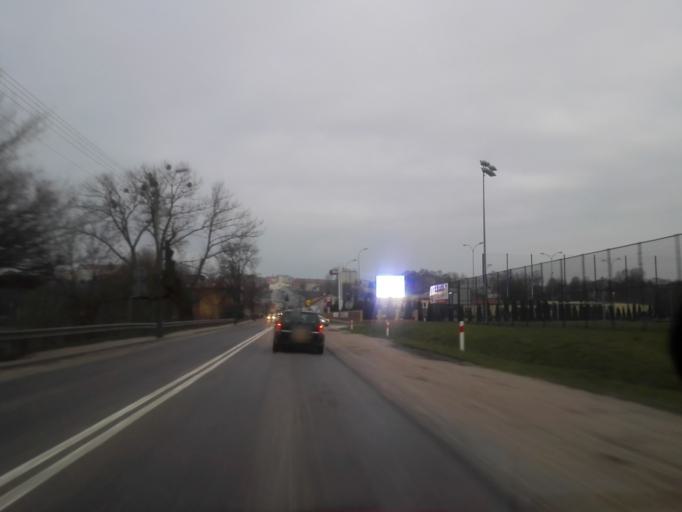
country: PL
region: Podlasie
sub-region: Powiat lomzynski
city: Piatnica
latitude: 53.1853
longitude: 22.0849
